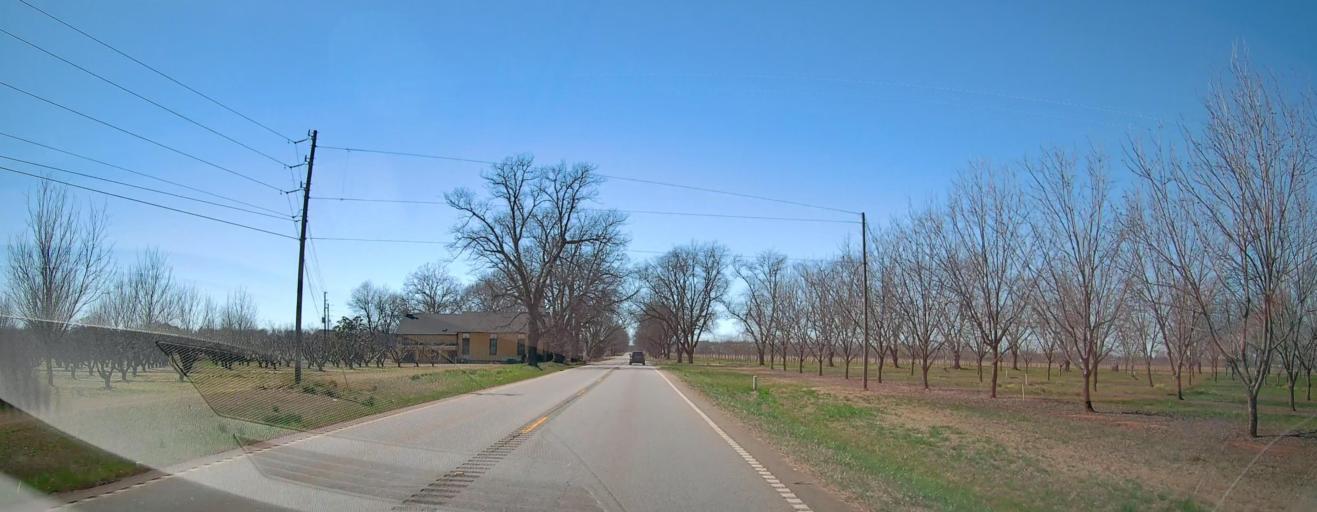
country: US
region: Georgia
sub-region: Peach County
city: Fort Valley
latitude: 32.5539
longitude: -83.8050
